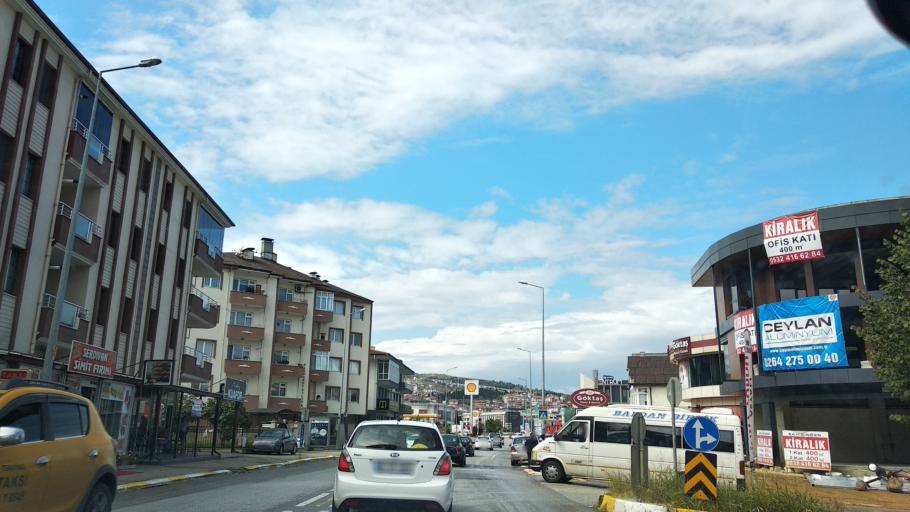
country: TR
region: Sakarya
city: Adapazari
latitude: 40.7583
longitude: 30.3678
